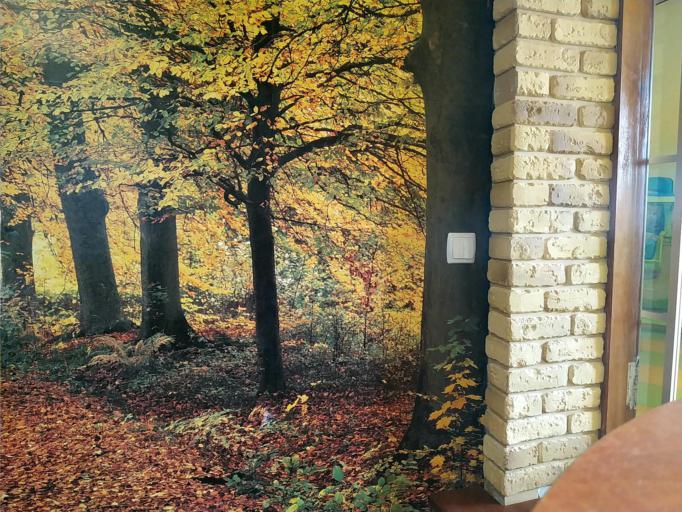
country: RU
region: Smolensk
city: Katyn'
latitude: 54.8561
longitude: 31.8330
